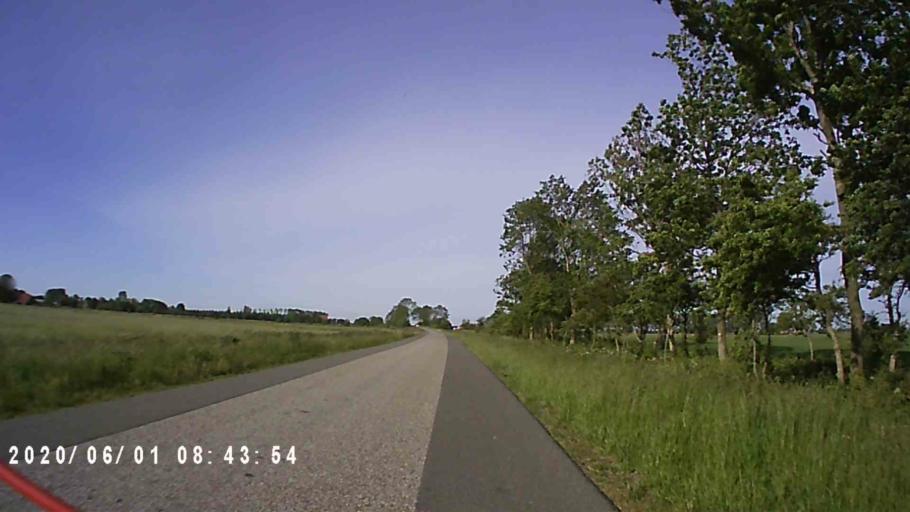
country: NL
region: Friesland
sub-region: Gemeente Ferwerderadiel
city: Burdaard
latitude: 53.2820
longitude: 5.8402
